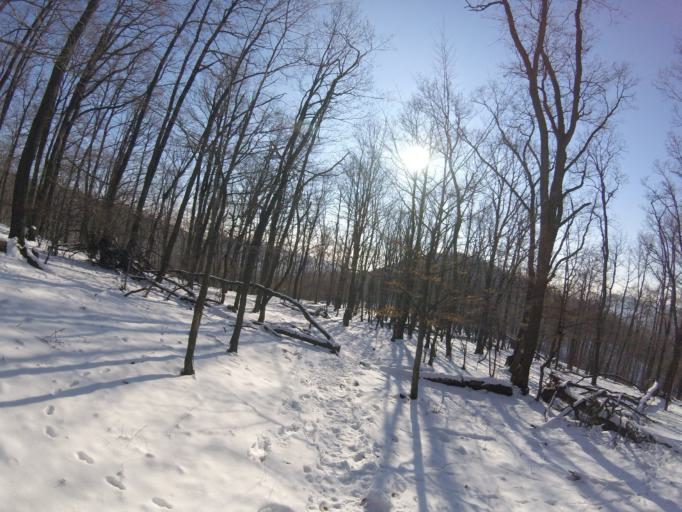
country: HU
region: Heves
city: Parad
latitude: 47.8678
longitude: 20.0567
